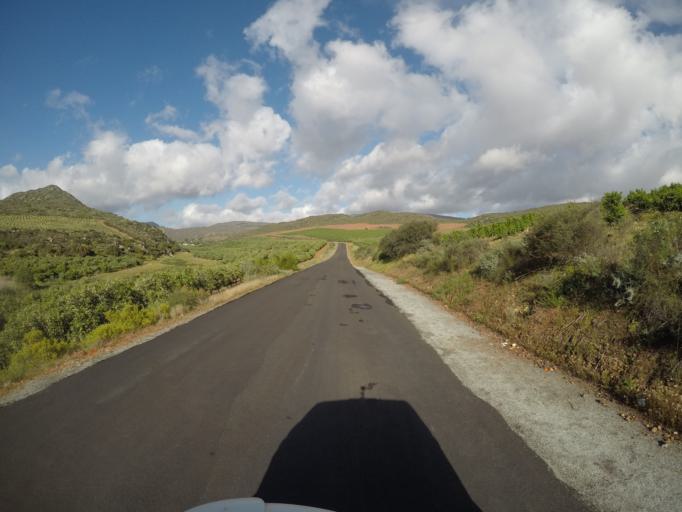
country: ZA
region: Western Cape
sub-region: West Coast District Municipality
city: Clanwilliam
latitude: -32.4305
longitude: 18.9521
